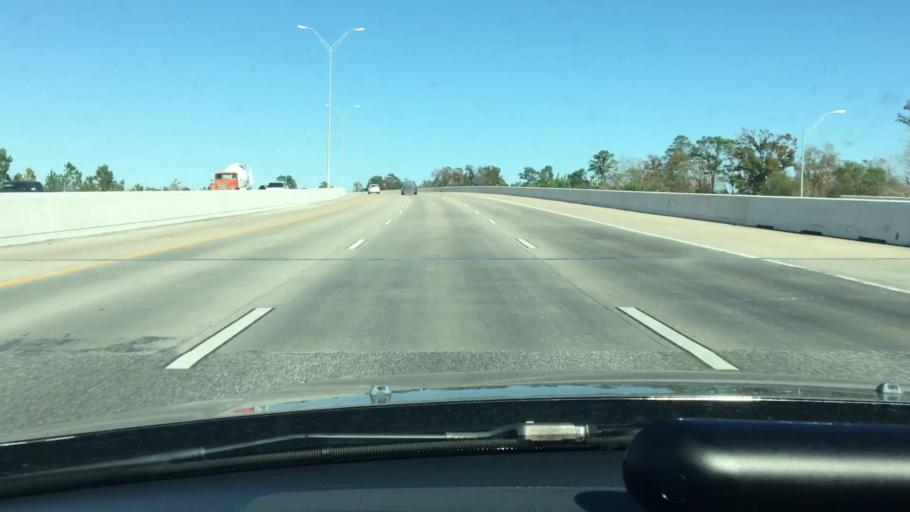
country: US
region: Texas
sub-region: Harris County
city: Atascocita
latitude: 29.9221
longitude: -95.1999
